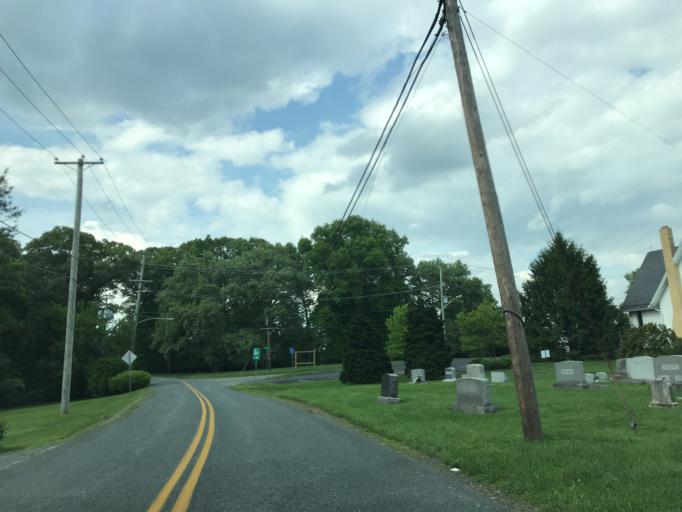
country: US
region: Pennsylvania
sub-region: York County
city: Susquehanna Trails
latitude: 39.6673
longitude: -76.3793
